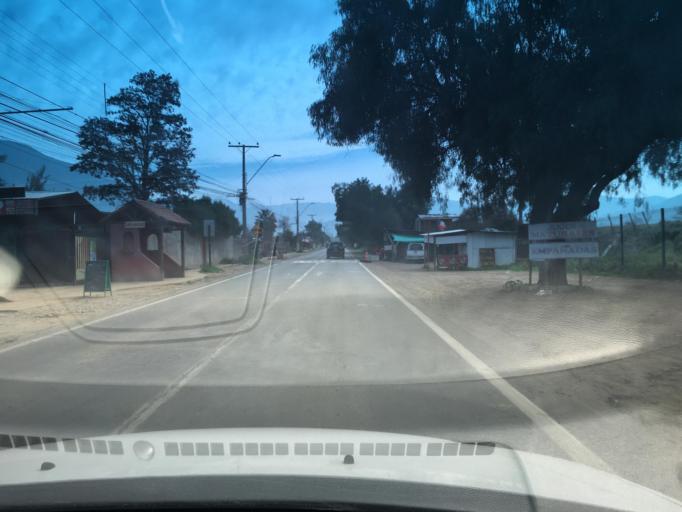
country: CL
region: Santiago Metropolitan
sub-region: Provincia de Chacabuco
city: Lampa
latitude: -33.0960
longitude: -70.9293
